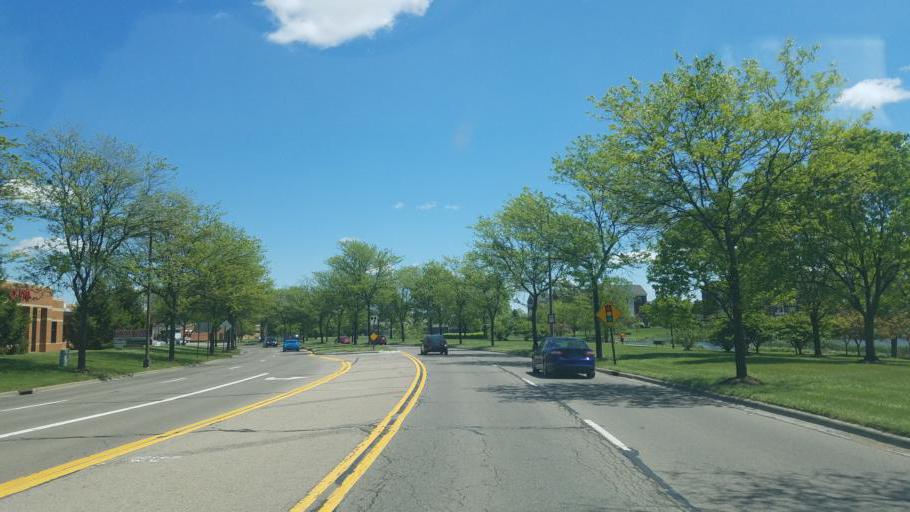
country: US
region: Ohio
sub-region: Franklin County
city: Hilliard
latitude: 40.0268
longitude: -83.1161
